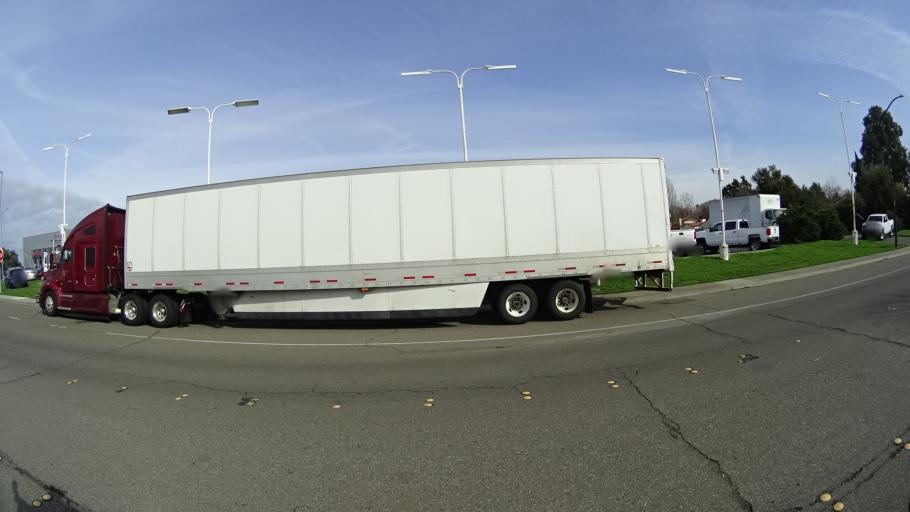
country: US
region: California
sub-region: Yolo County
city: Davis
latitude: 38.5515
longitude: -121.6915
